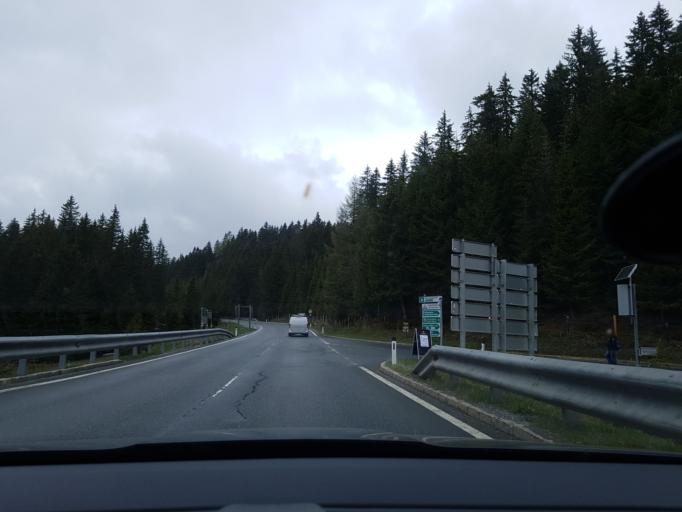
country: AT
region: Salzburg
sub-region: Politischer Bezirk Zell am See
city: Krimml
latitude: 47.2434
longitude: 12.1211
